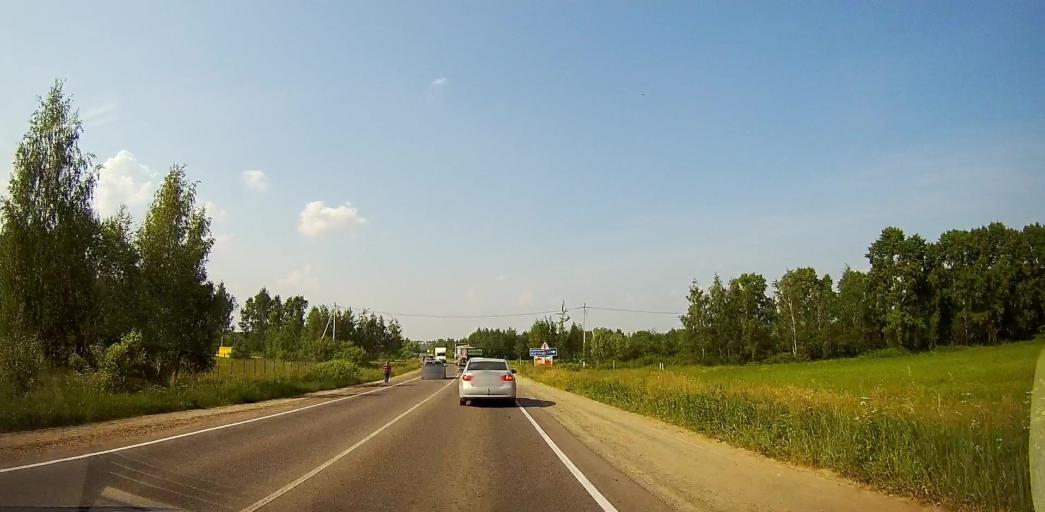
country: RU
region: Moskovskaya
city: Zhitnevo
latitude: 55.3203
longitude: 37.9001
